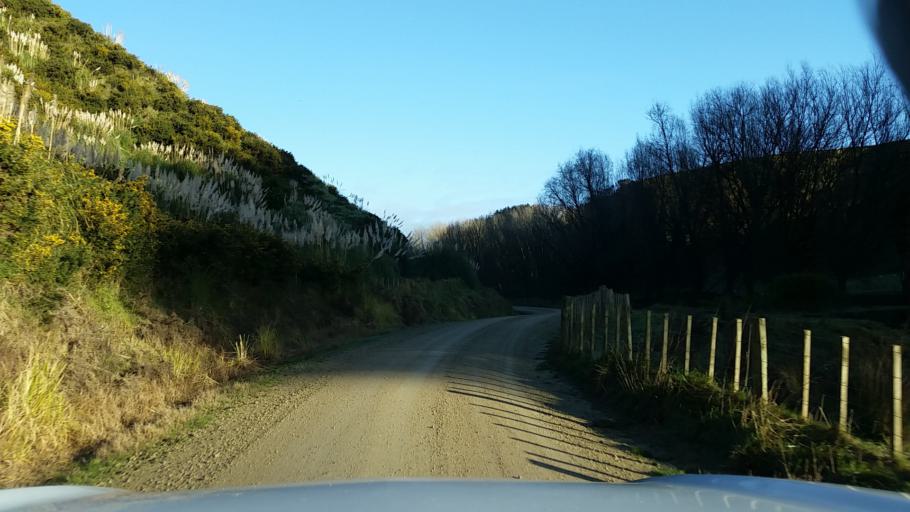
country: NZ
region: Taranaki
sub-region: South Taranaki District
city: Patea
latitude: -39.7597
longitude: 174.7330
